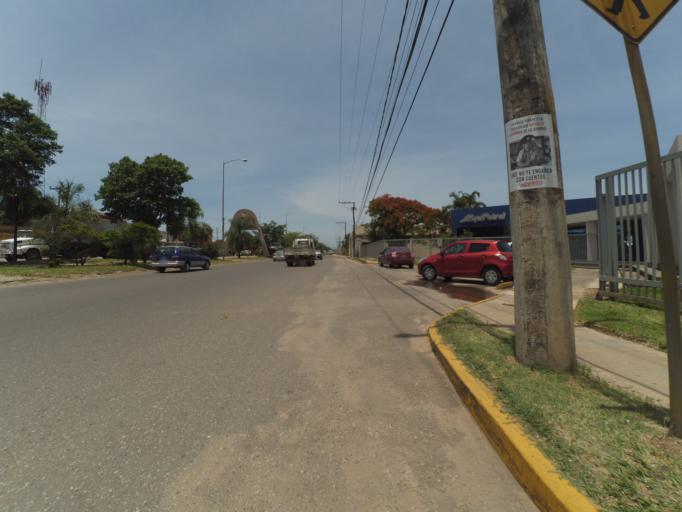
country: BO
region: Santa Cruz
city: Santa Cruz de la Sierra
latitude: -17.8416
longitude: -63.2421
